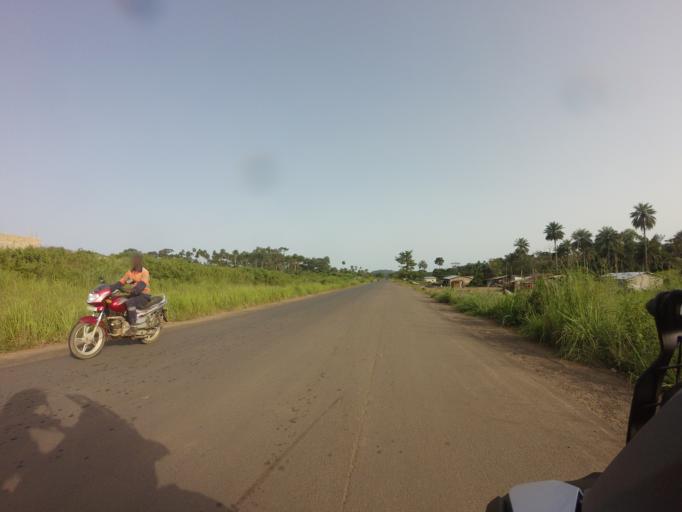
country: GN
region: Nzerekore
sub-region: Nzerekore Prefecture
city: Nzerekore
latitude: 8.0308
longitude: -9.0170
